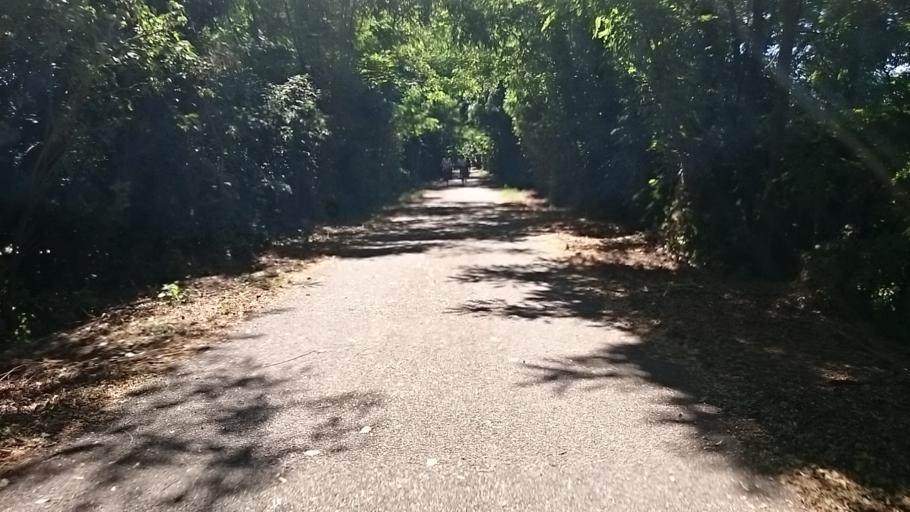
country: IT
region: Veneto
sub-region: Provincia di Padova
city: Torreselle
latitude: 45.6066
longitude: 12.0192
